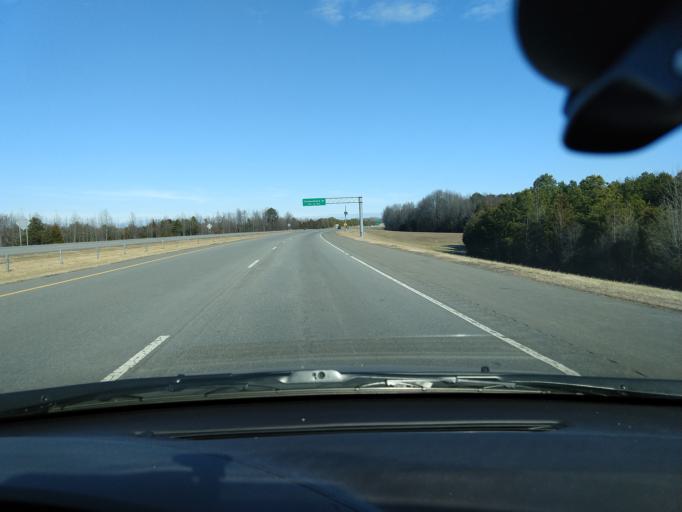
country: US
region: North Carolina
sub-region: Guilford County
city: Oak Ridge
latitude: 36.0958
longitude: -79.9664
